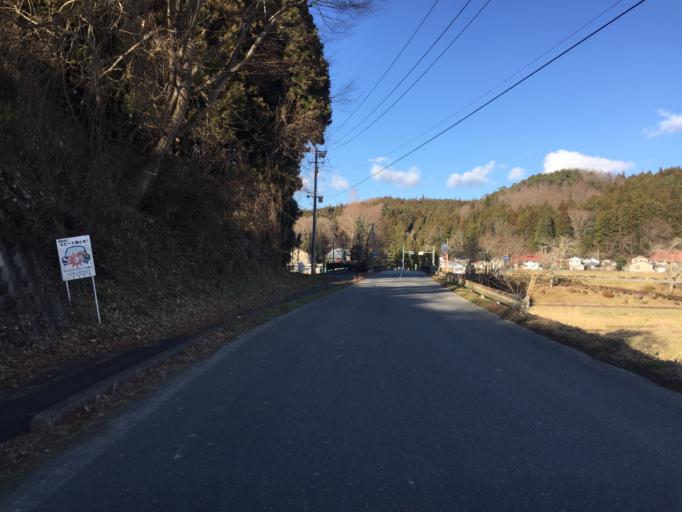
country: JP
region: Fukushima
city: Funehikimachi-funehiki
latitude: 37.2558
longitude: 140.6529
